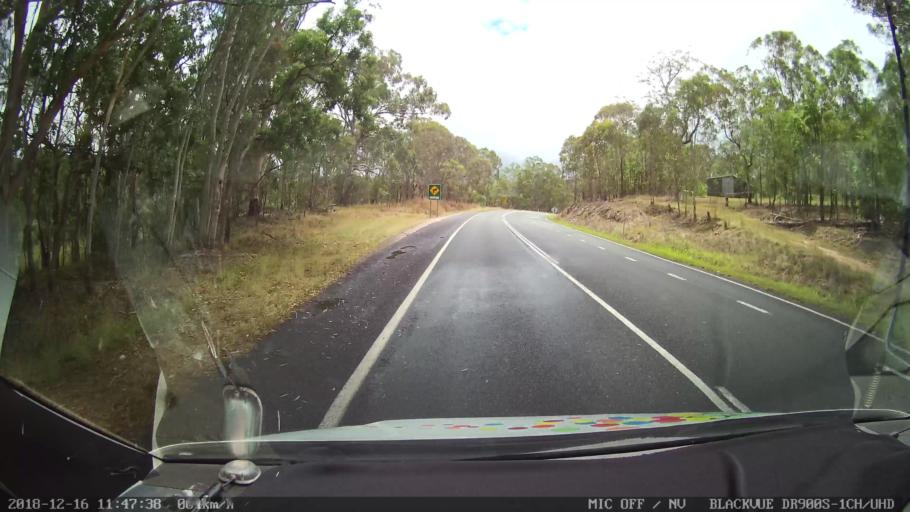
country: AU
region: New South Wales
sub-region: Tenterfield Municipality
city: Carrolls Creek
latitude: -28.9206
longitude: 152.2400
